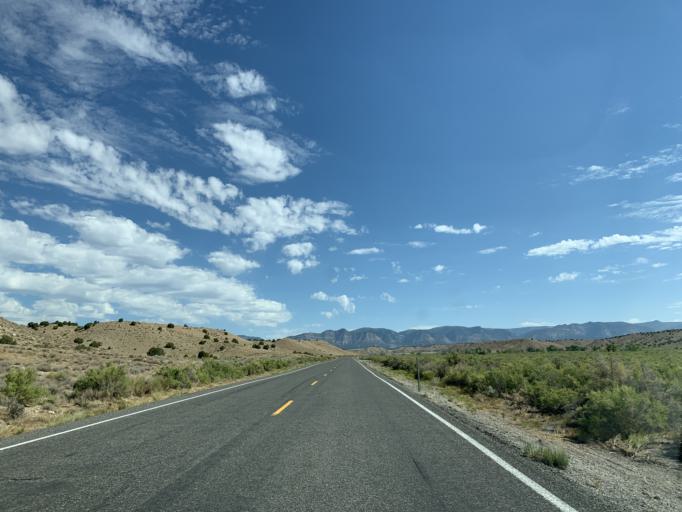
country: US
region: Utah
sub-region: Carbon County
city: Wellington
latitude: 39.5854
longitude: -110.6477
